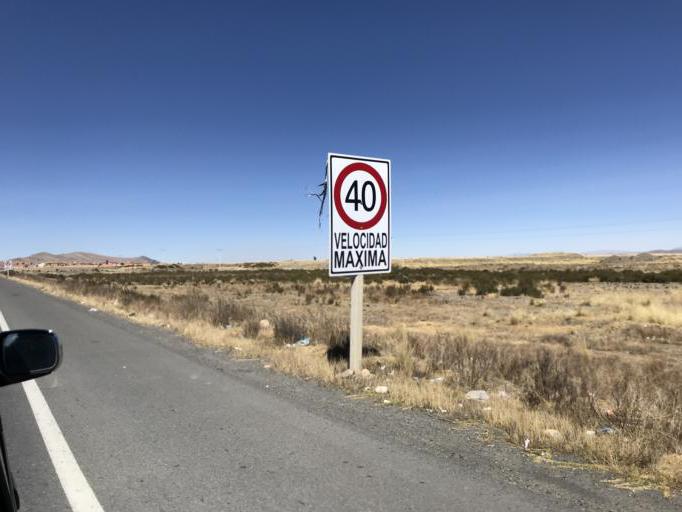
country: BO
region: La Paz
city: Batallas
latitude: -16.3222
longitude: -68.4329
